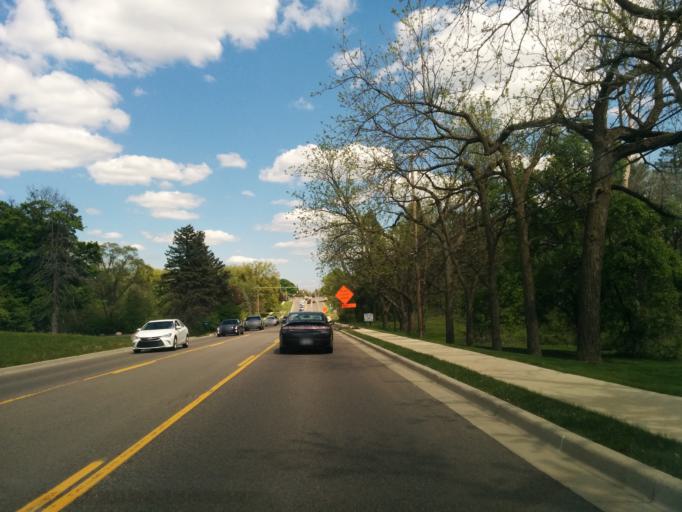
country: US
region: Michigan
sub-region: Oakland County
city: Franklin
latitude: 42.5141
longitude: -83.3449
